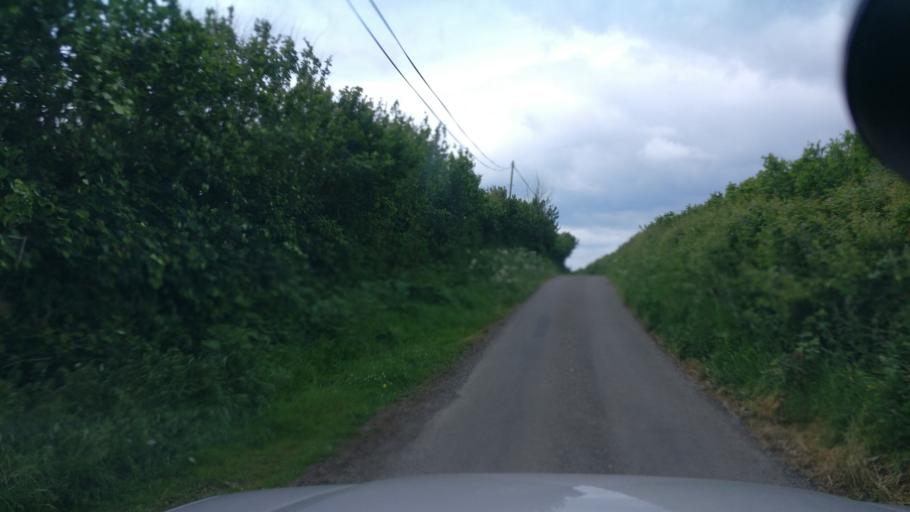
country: IE
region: Connaught
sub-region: County Galway
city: Ballinasloe
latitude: 53.2920
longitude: -8.3179
